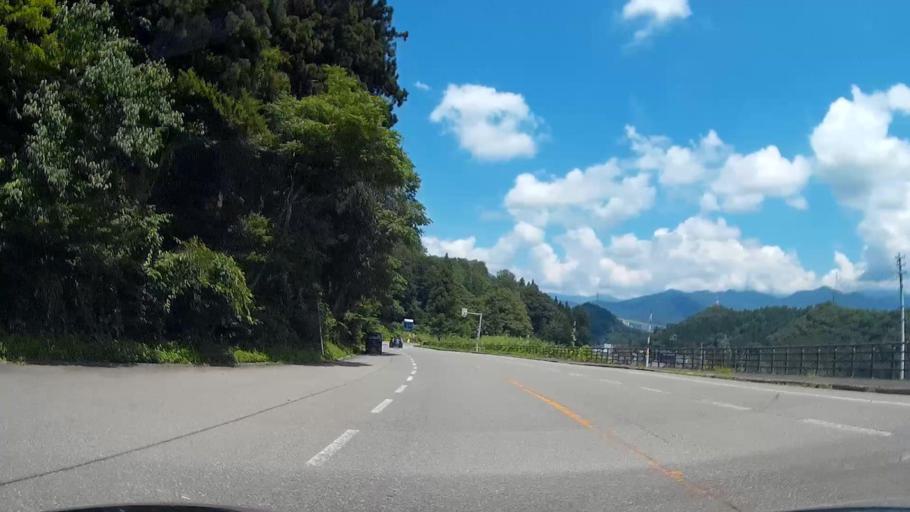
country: JP
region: Niigata
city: Shiozawa
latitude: 36.9147
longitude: 138.8026
